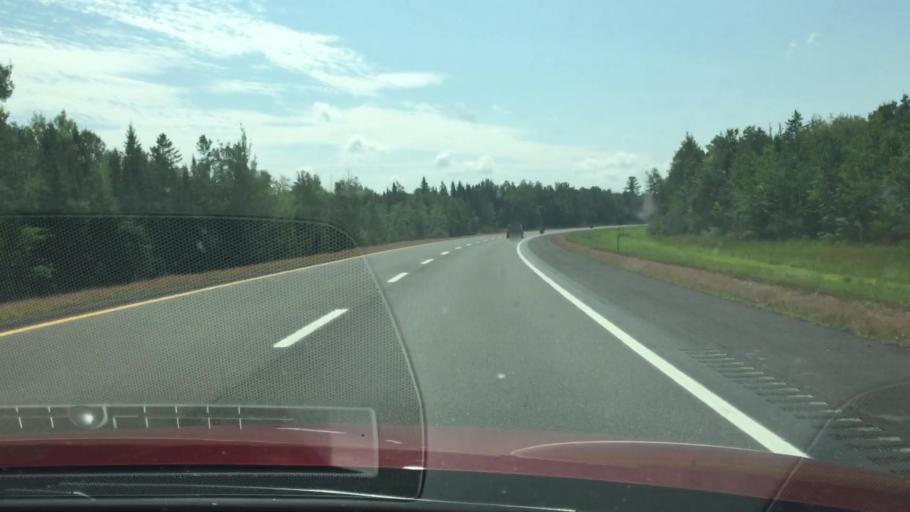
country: US
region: Maine
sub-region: Penobscot County
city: Patten
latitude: 45.9935
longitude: -68.2798
